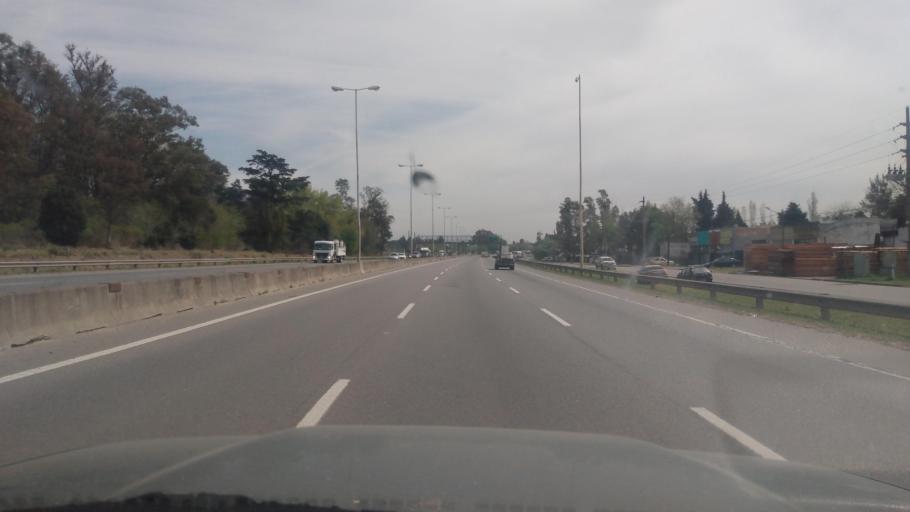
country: AR
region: Buenos Aires
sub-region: Partido de Pilar
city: Pilar
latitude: -34.4377
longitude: -58.9815
